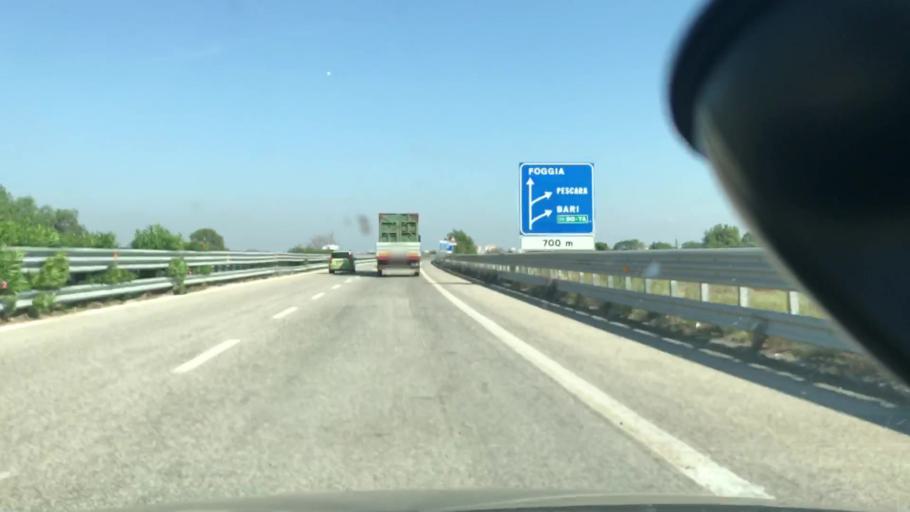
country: IT
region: Apulia
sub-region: Provincia di Foggia
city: Foggia
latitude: 41.4168
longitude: 15.5585
